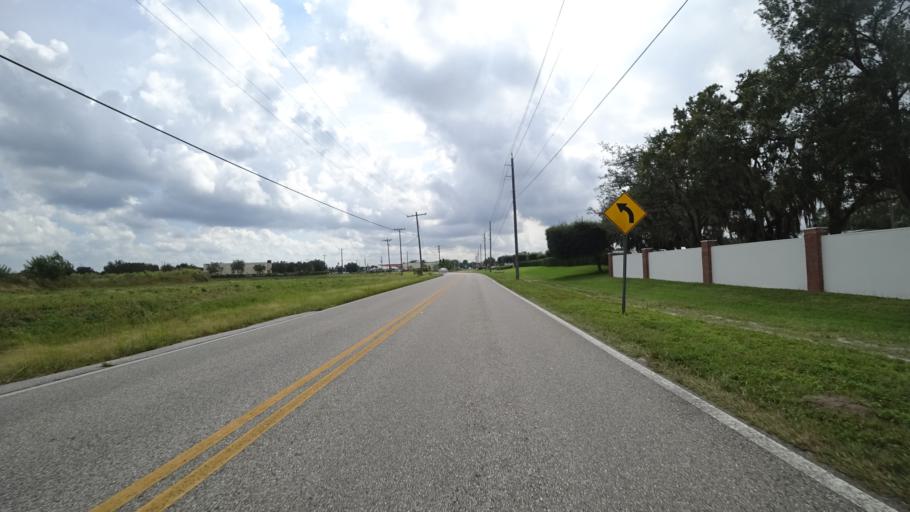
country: US
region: Florida
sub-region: Manatee County
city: Ellenton
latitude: 27.5455
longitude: -82.4787
